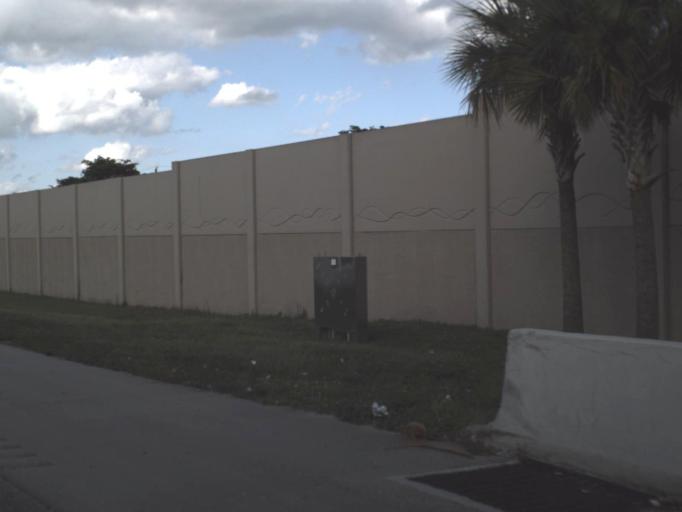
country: US
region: Florida
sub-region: Broward County
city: Lauderdale Lakes
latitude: 26.1659
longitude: -80.2196
